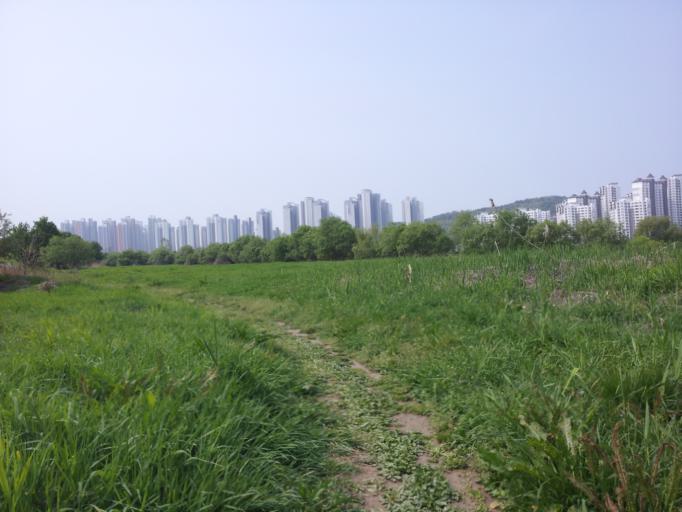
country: KR
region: Daejeon
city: Daejeon
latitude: 36.3233
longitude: 127.3535
